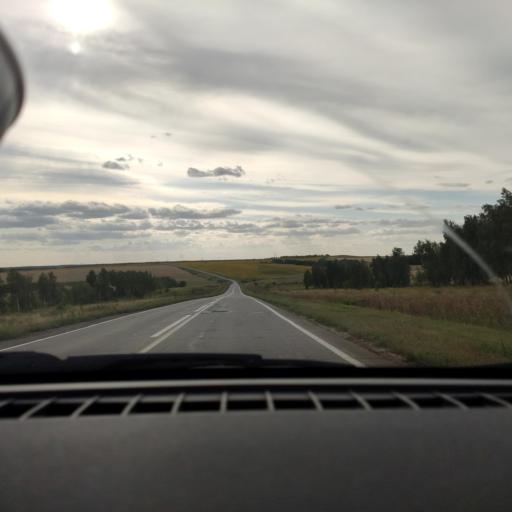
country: RU
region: Samara
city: Kinel'
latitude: 53.4412
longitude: 50.6246
